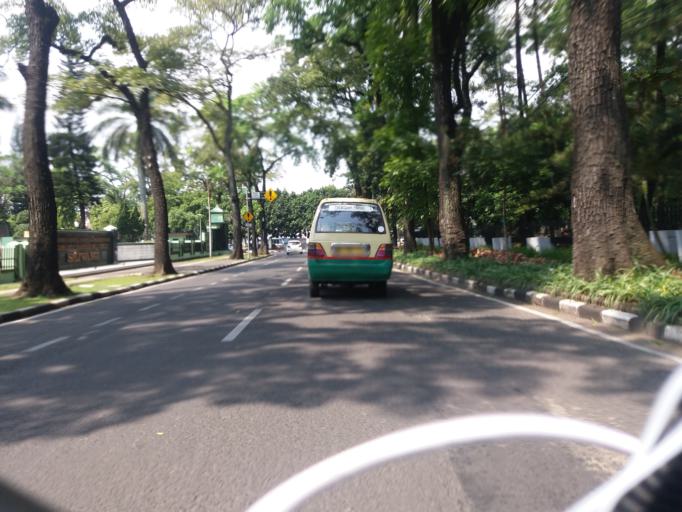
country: ID
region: West Java
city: Bandung
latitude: -6.9103
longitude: 107.6133
